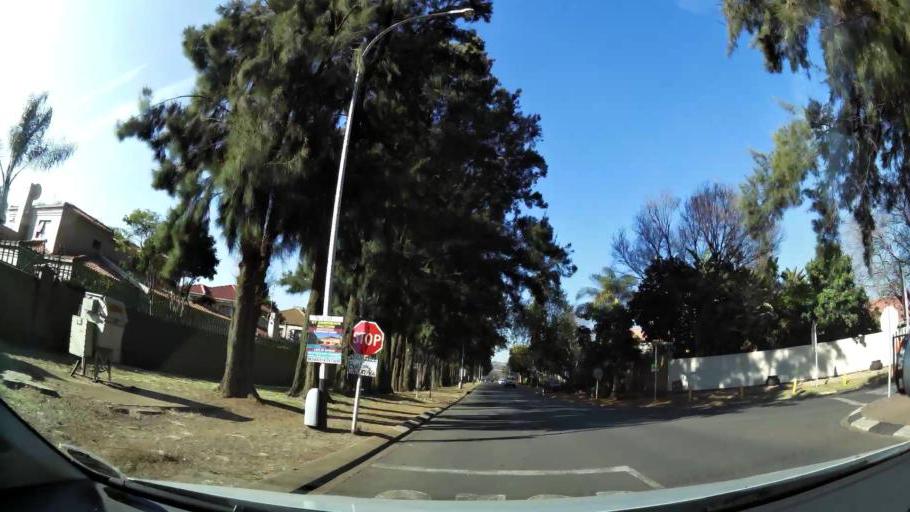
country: ZA
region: Gauteng
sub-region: City of Johannesburg Metropolitan Municipality
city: Modderfontein
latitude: -26.1615
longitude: 28.1427
